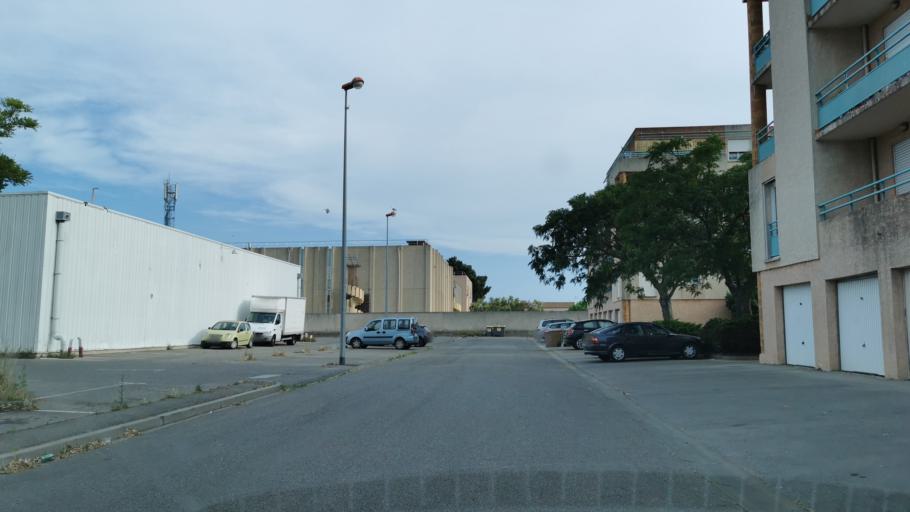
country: FR
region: Languedoc-Roussillon
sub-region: Departement de l'Aude
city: Narbonne
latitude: 43.1856
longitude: 2.9926
